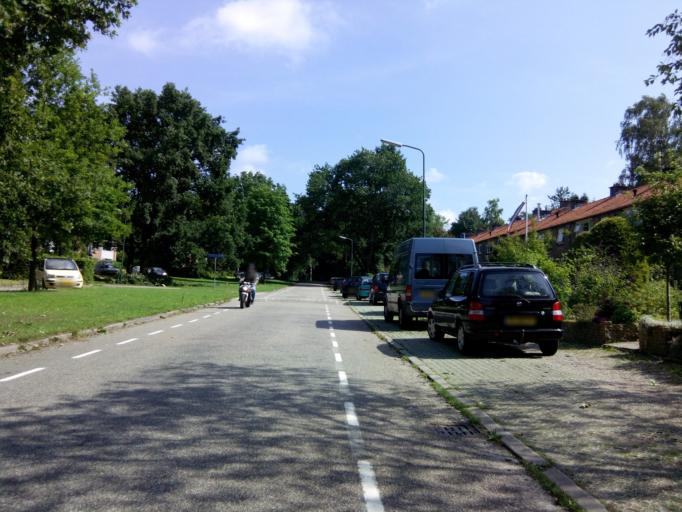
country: NL
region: Utrecht
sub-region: Gemeente Utrechtse Heuvelrug
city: Doorn
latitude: 52.0443
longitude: 5.3424
